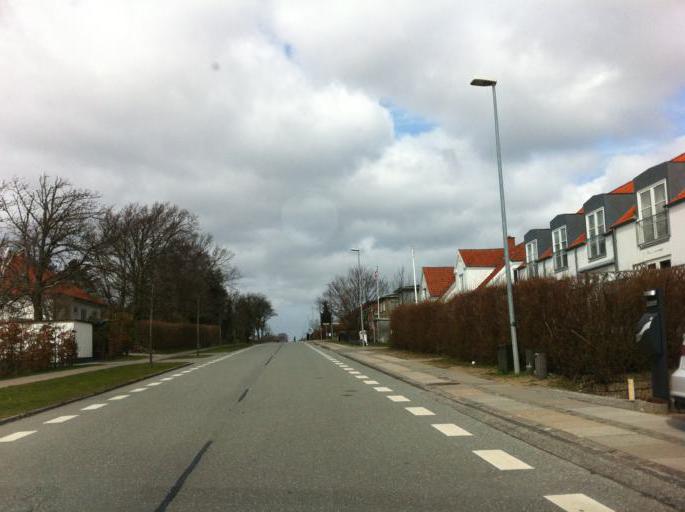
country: DK
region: Central Jutland
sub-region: Syddjurs Kommune
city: Ebeltoft
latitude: 56.2036
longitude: 10.6821
